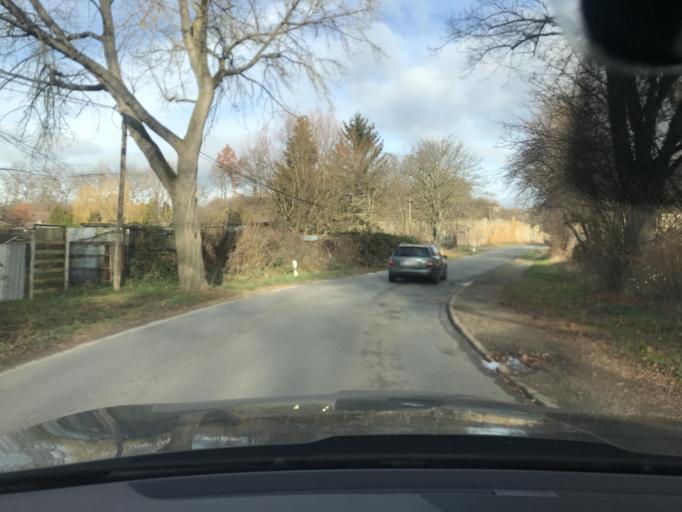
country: DE
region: Saxony-Anhalt
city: Quedlinburg
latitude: 51.7834
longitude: 11.1273
